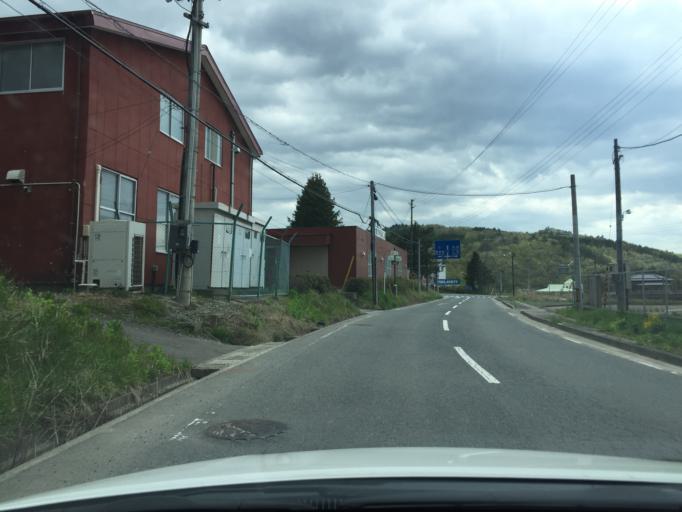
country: JP
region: Miyagi
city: Marumori
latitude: 37.6953
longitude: 140.7595
